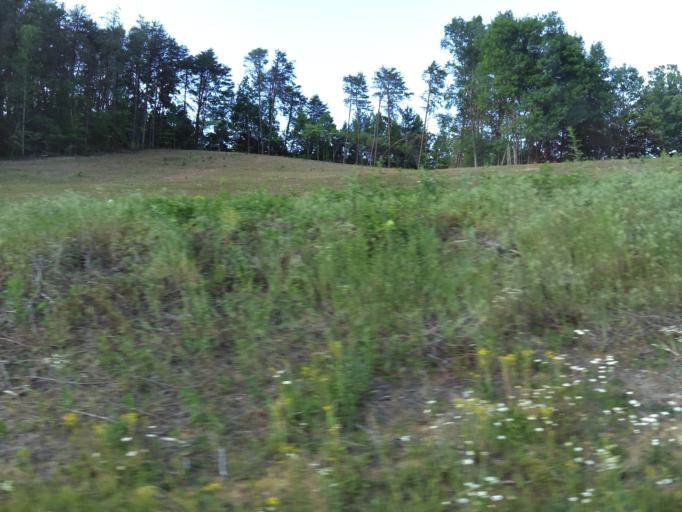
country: US
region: Tennessee
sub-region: Sevier County
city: Sevierville
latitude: 35.8312
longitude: -83.6137
